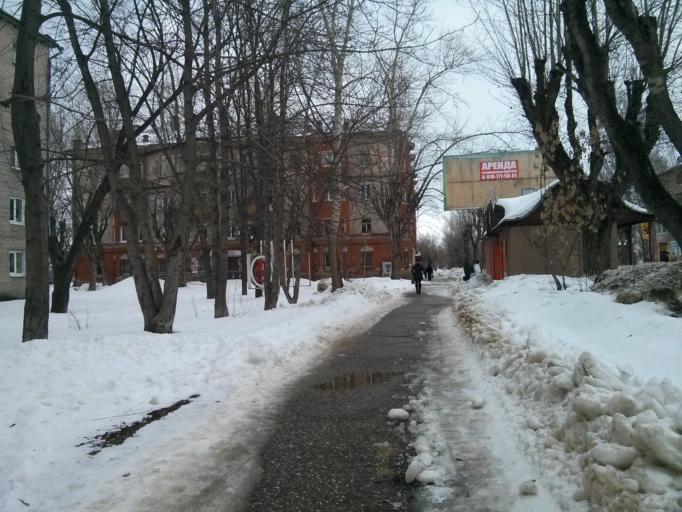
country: RU
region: Vladimir
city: Murom
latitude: 55.5652
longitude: 42.0575
